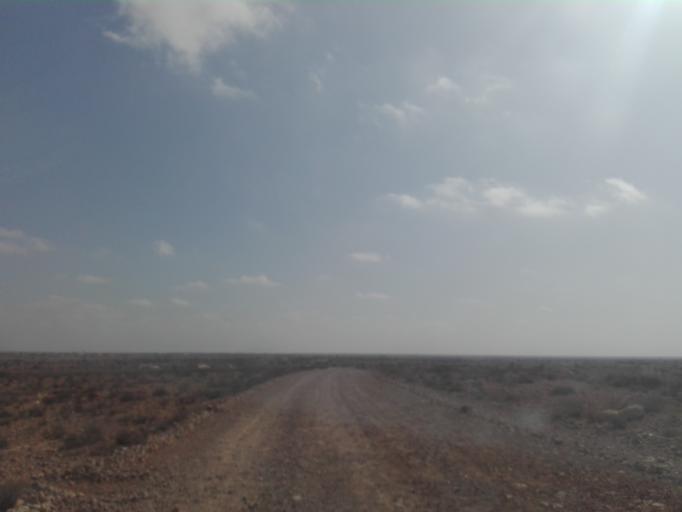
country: TN
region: Madanin
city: Medenine
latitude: 33.4318
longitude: 10.4119
